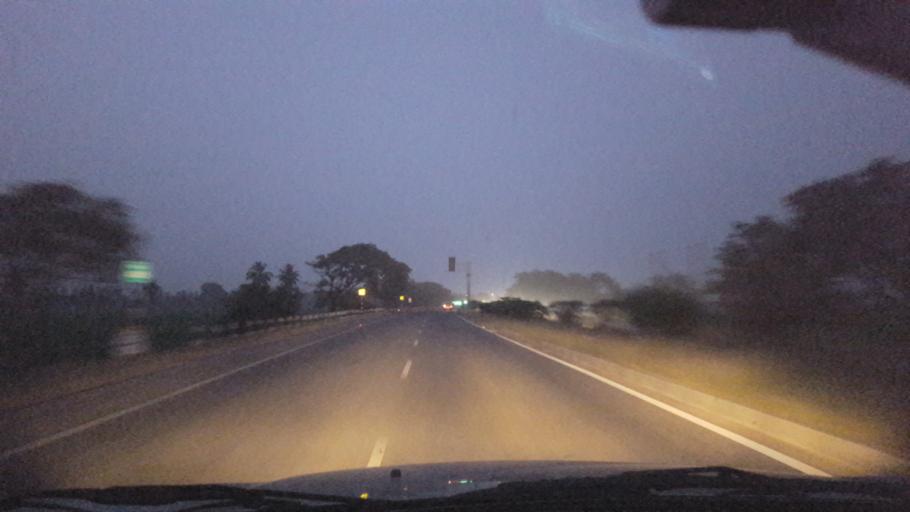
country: IN
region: Andhra Pradesh
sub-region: East Godavari
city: Rajahmundry
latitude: 17.1141
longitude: 81.9244
